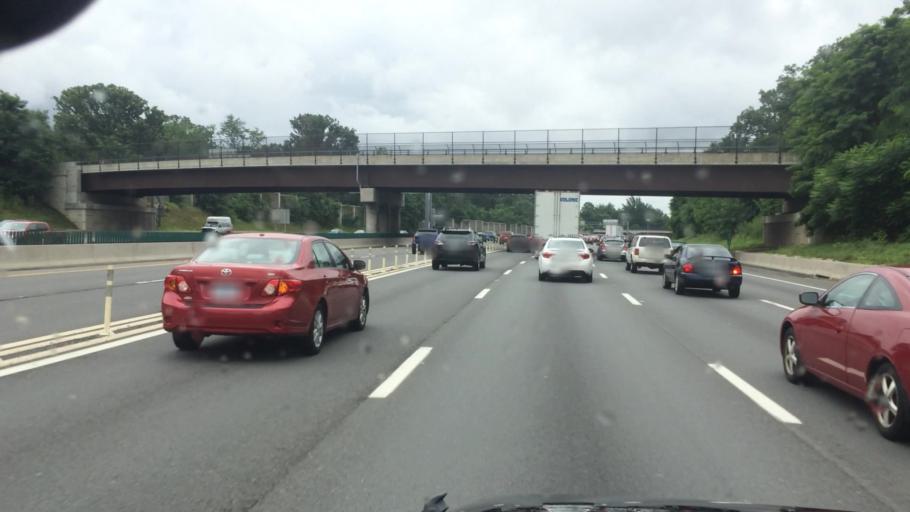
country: US
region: Virginia
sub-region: Fairfax County
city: Idylwood
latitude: 38.8989
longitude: -77.2151
